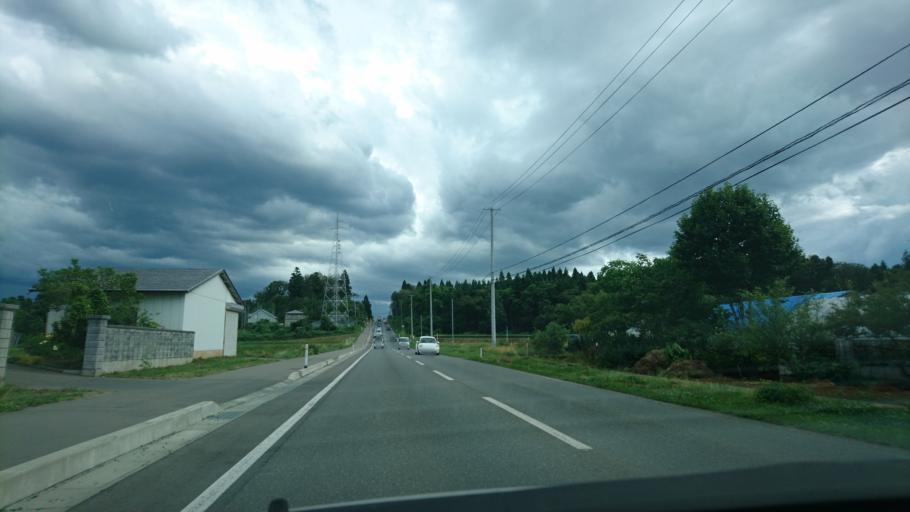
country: JP
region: Iwate
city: Kitakami
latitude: 39.3113
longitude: 141.1272
